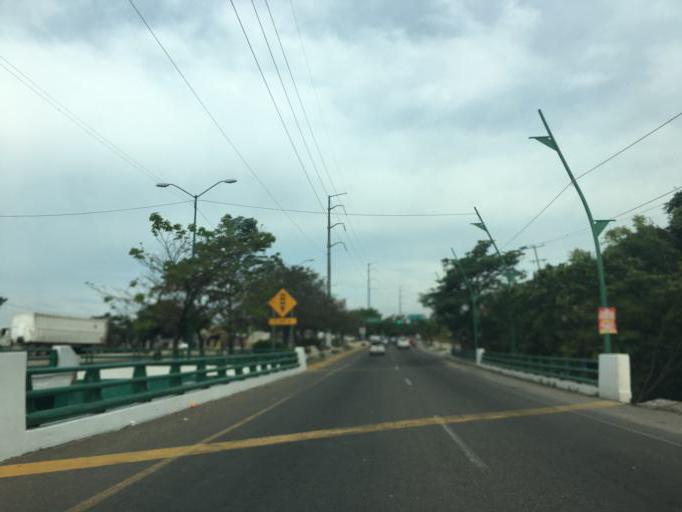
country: MX
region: Chiapas
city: Tuxtla Gutierrez
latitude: 16.7754
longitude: -93.1766
